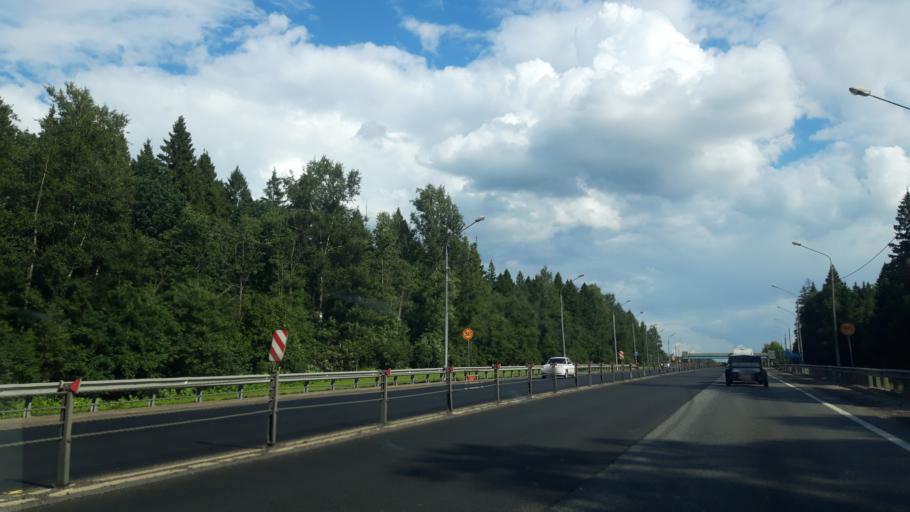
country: RU
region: Moskovskaya
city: Klin
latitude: 56.2760
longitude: 36.8345
